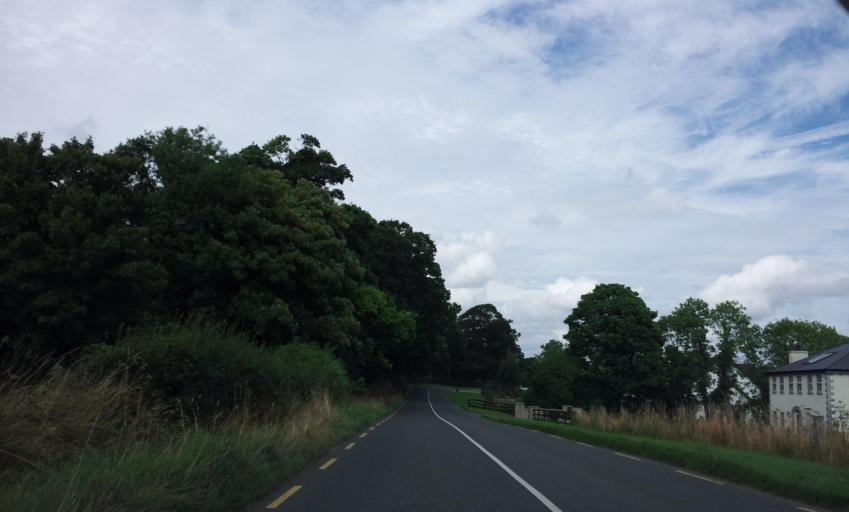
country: IE
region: Leinster
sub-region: Laois
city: Stradbally
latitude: 52.9756
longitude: -7.2135
